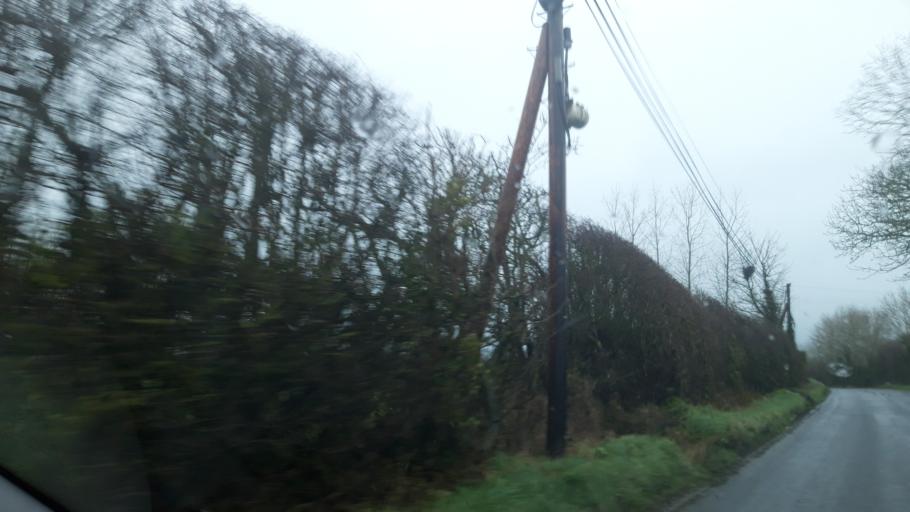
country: IE
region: Leinster
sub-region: Kilkenny
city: Kilkenny
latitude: 52.6661
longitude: -7.2197
